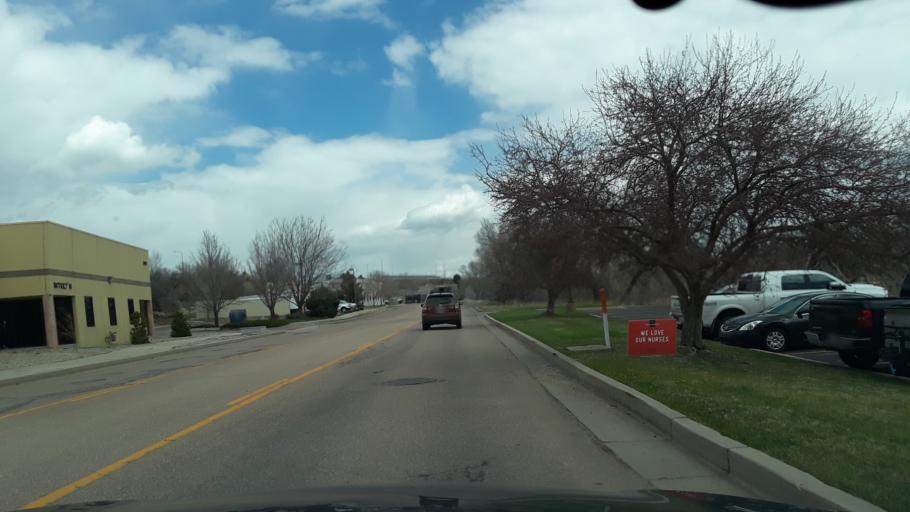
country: US
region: Colorado
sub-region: El Paso County
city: Colorado Springs
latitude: 38.9051
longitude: -104.8242
